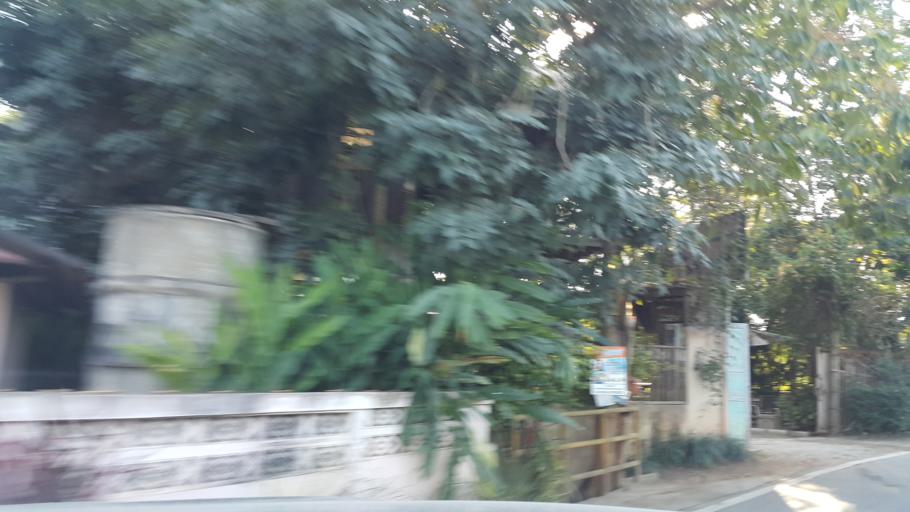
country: TH
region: Chiang Mai
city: Chiang Mai
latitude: 18.7683
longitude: 98.9517
